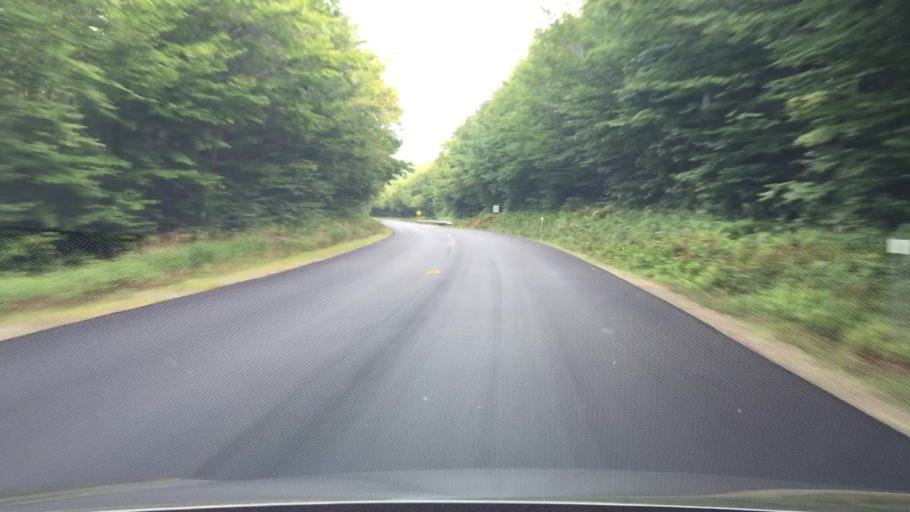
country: US
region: New Hampshire
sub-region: Carroll County
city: Sandwich
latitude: 44.0172
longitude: -71.4329
